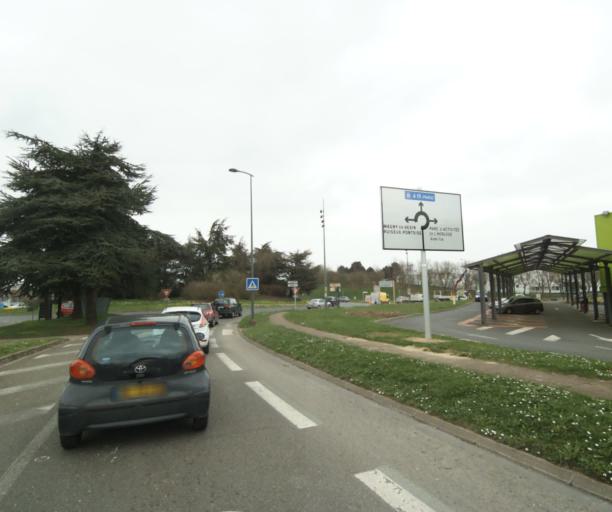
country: FR
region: Ile-de-France
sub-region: Departement du Val-d'Oise
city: Vaureal
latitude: 49.0535
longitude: 2.0245
